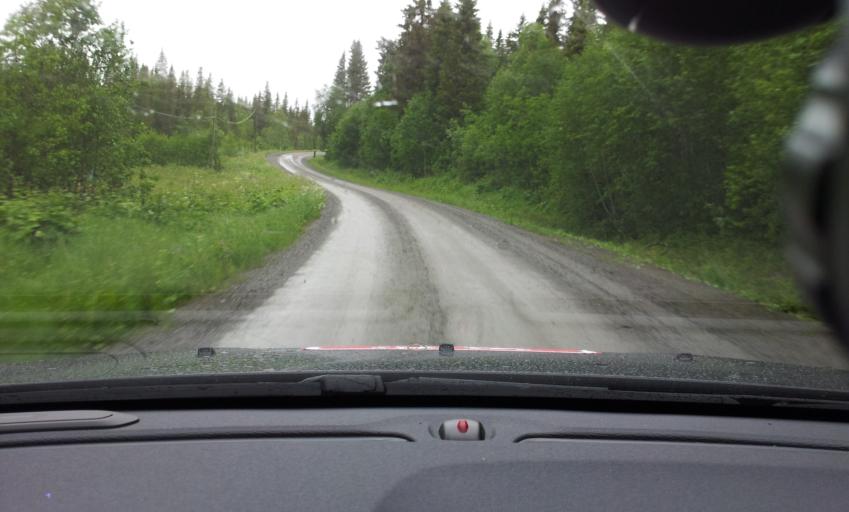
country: SE
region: Jaemtland
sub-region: Are Kommun
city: Are
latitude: 63.5005
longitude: 12.7568
